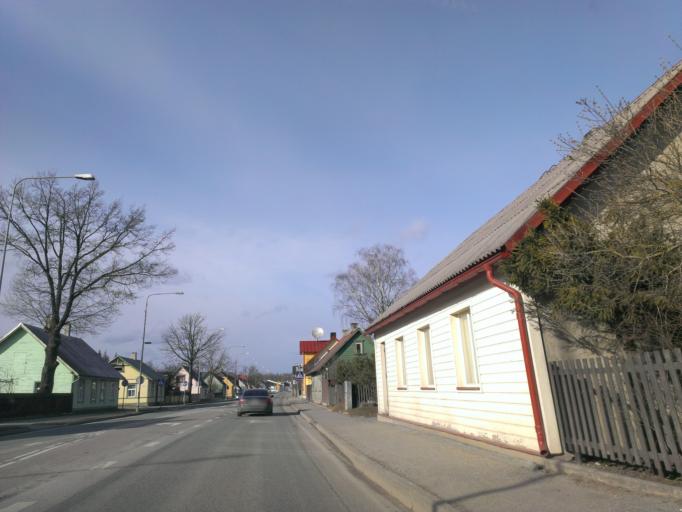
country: EE
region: Paernumaa
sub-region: Paernu linn
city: Parnu
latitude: 58.3996
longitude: 24.4932
